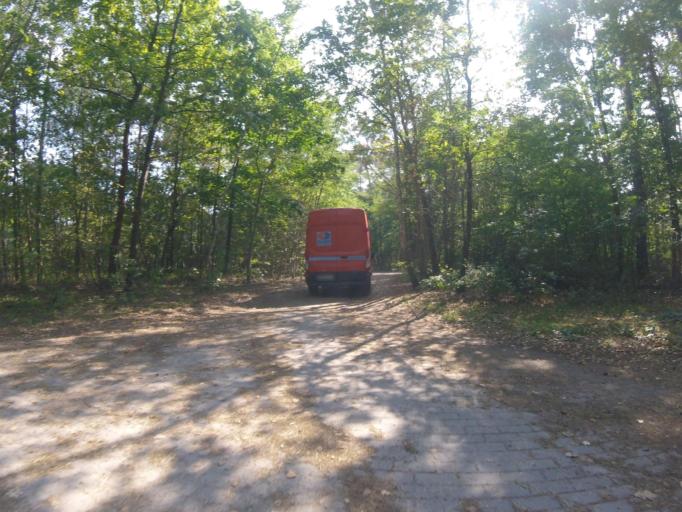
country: DE
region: Brandenburg
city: Bestensee
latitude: 52.2716
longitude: 13.7477
